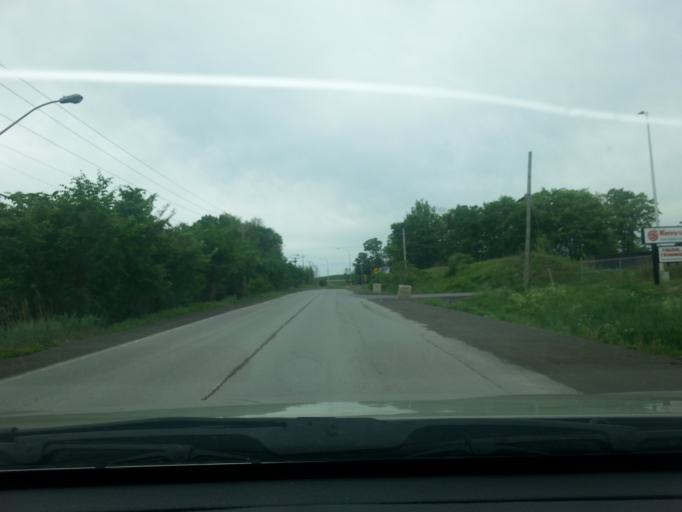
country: CA
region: Quebec
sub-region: Lanaudiere
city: Terrebonne
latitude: 45.6606
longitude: -73.6390
